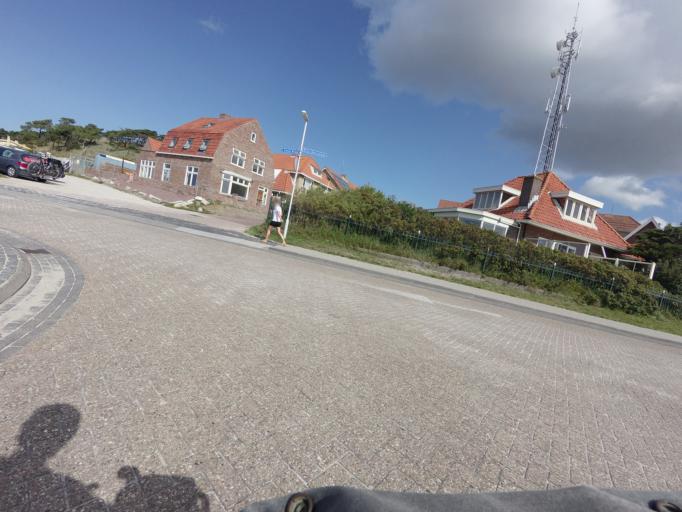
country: NL
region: Friesland
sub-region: Gemeente Terschelling
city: West-Terschelling
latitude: 53.3563
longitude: 5.2124
